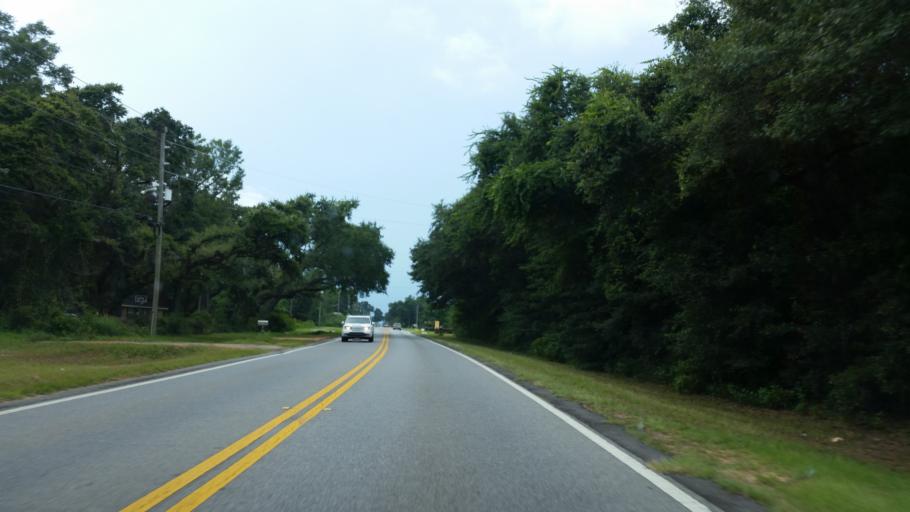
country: US
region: Florida
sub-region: Santa Rosa County
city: Pace
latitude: 30.6230
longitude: -87.1624
